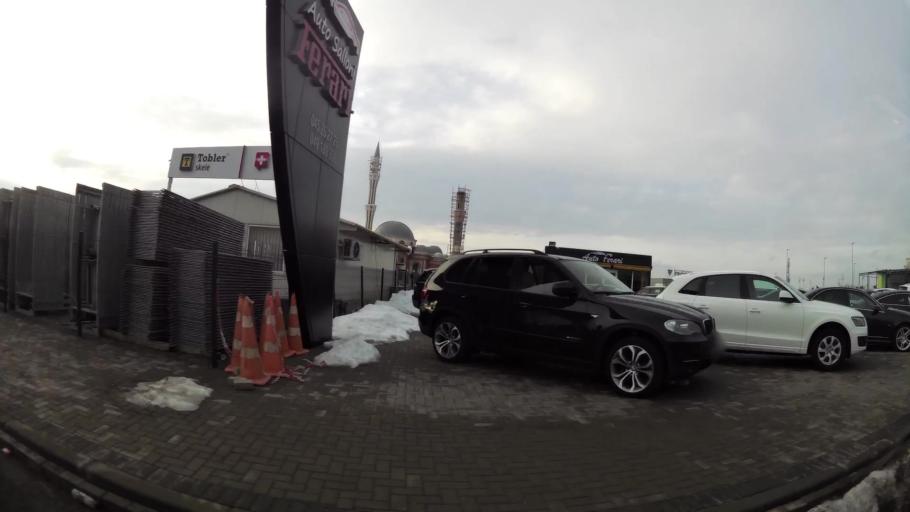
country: XK
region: Pristina
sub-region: Komuna e Prishtines
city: Pristina
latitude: 42.6328
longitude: 21.1508
